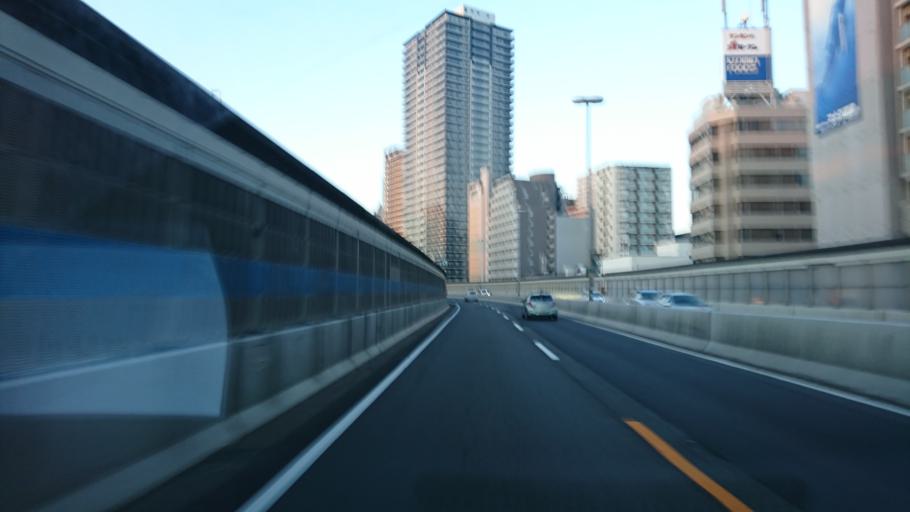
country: JP
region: Hyogo
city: Kobe
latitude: 34.6848
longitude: 135.1847
